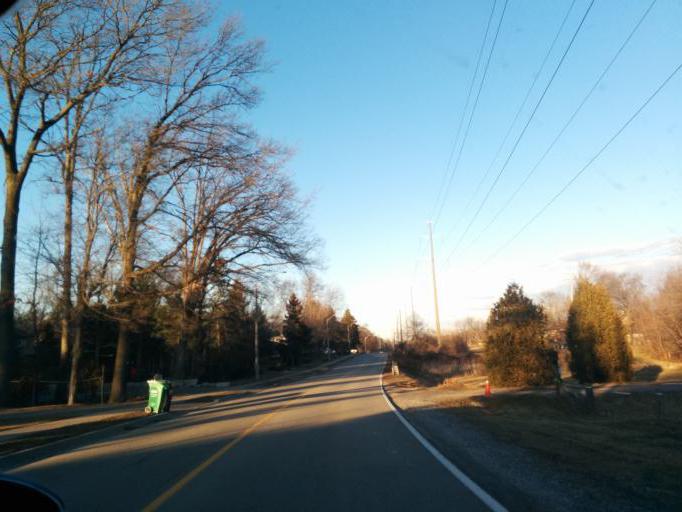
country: CA
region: Ontario
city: Mississauga
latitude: 43.5649
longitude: -79.6047
